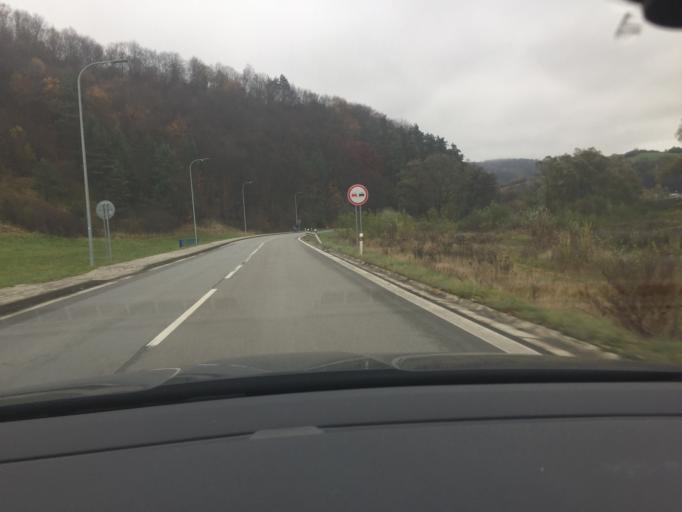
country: PL
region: Lesser Poland Voivodeship
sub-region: Powiat nowosadecki
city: Tylicz
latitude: 49.3186
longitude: 21.1219
